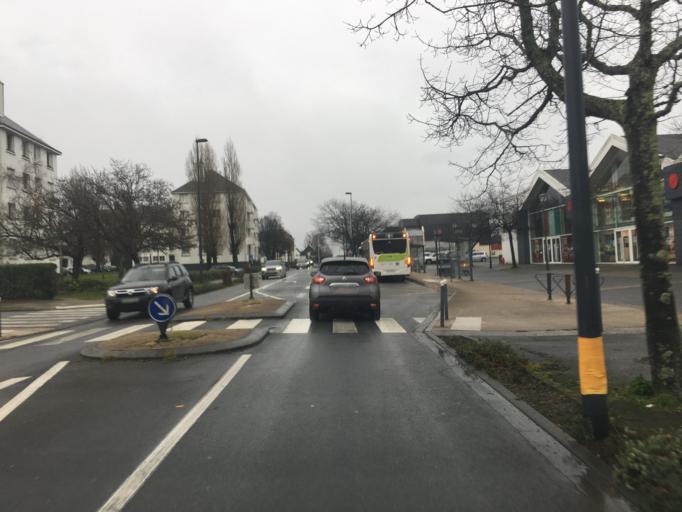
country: FR
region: Pays de la Loire
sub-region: Departement de la Loire-Atlantique
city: Guerande
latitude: 47.3311
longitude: -2.4262
